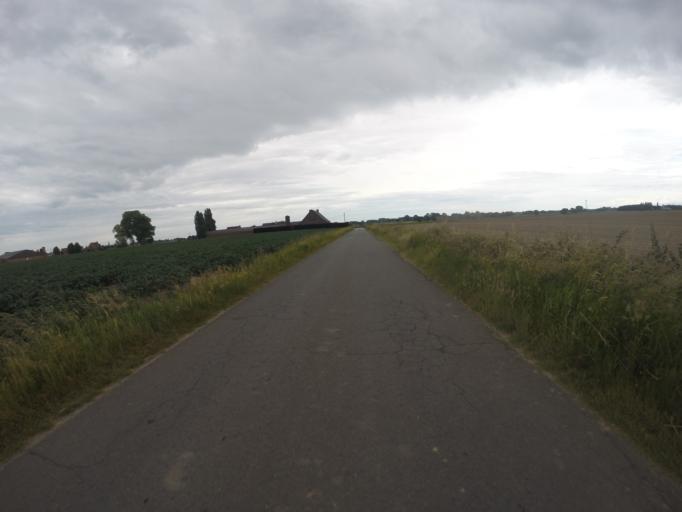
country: BE
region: Flanders
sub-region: Provincie West-Vlaanderen
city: Ruiselede
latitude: 51.0426
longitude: 3.3610
